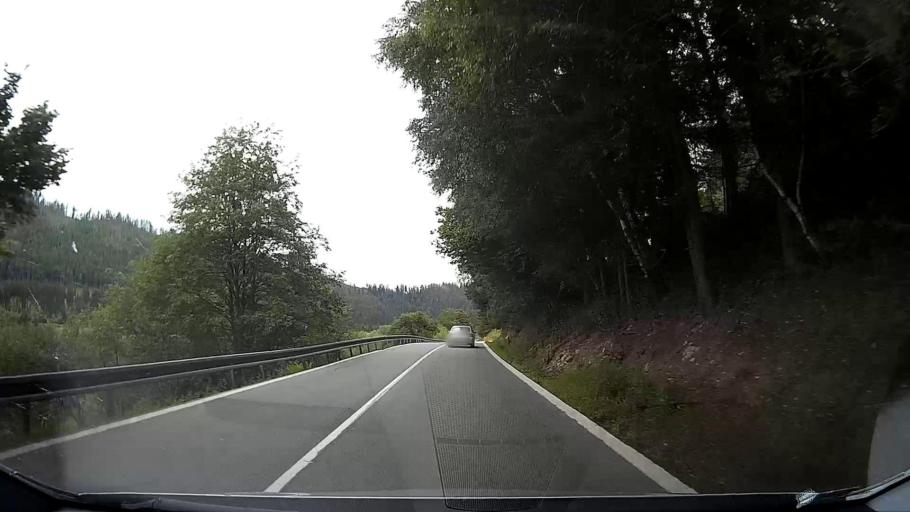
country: SK
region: Banskobystricky
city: Revuca
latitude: 48.8315
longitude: 20.1706
